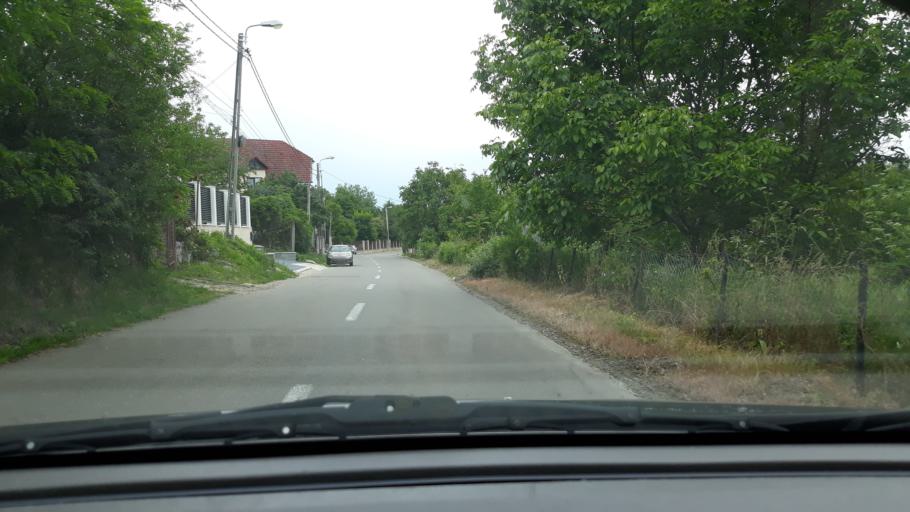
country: RO
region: Bihor
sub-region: Comuna Sanmartin
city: Sanmartin
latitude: 47.0520
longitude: 21.9805
